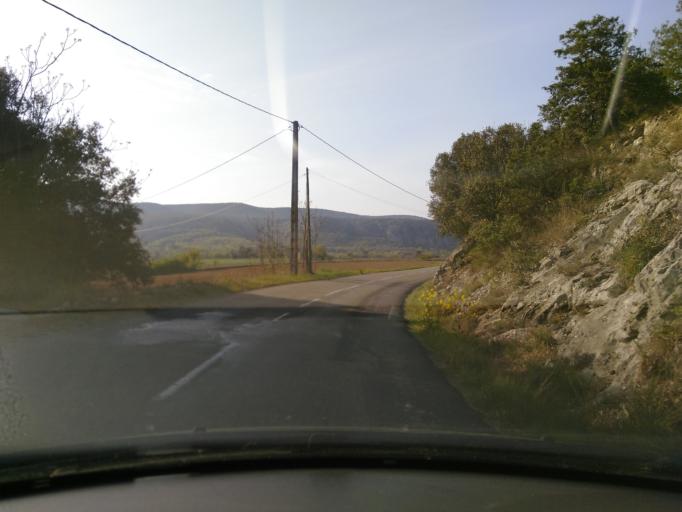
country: FR
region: Rhone-Alpes
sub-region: Departement de l'Ardeche
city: Ruoms
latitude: 44.4295
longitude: 4.4157
